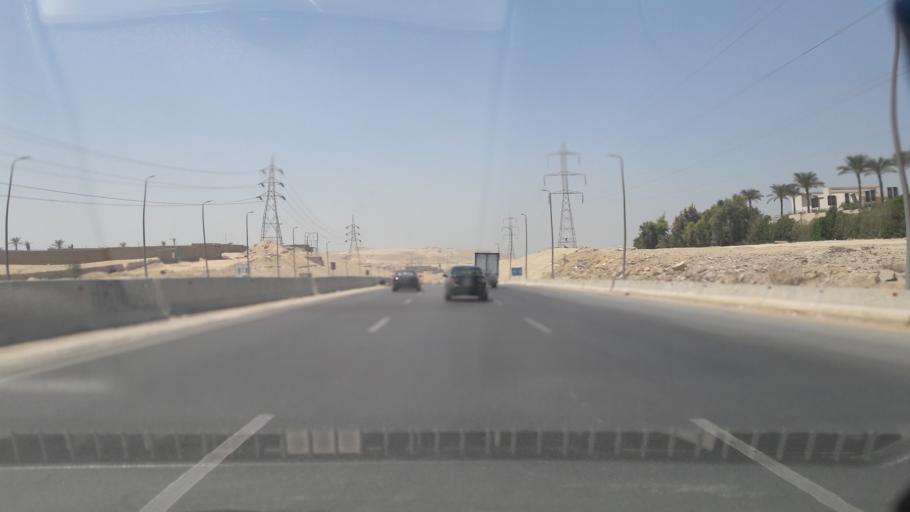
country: EG
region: Al Jizah
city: Awsim
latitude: 30.0091
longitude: 31.0868
